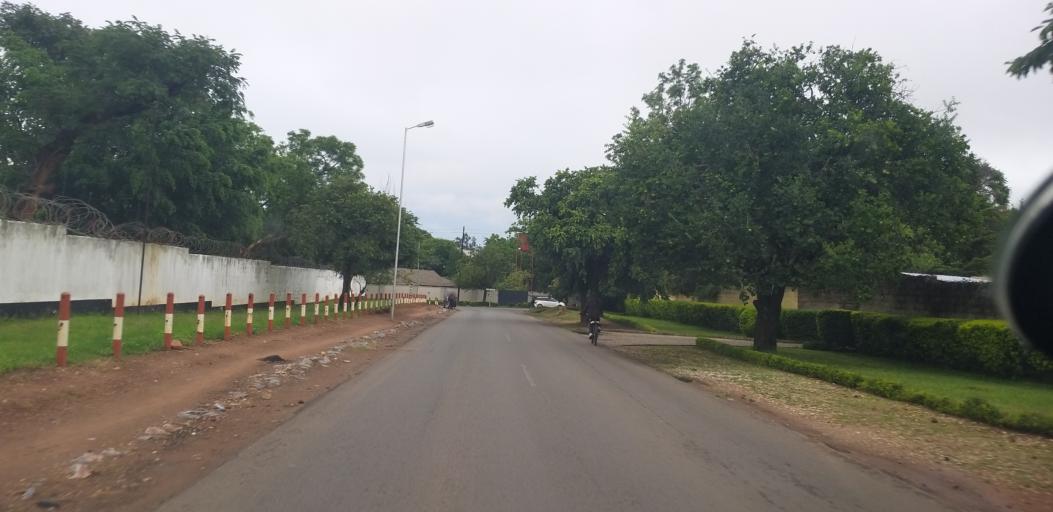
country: ZM
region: Lusaka
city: Lusaka
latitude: -15.4257
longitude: 28.3355
